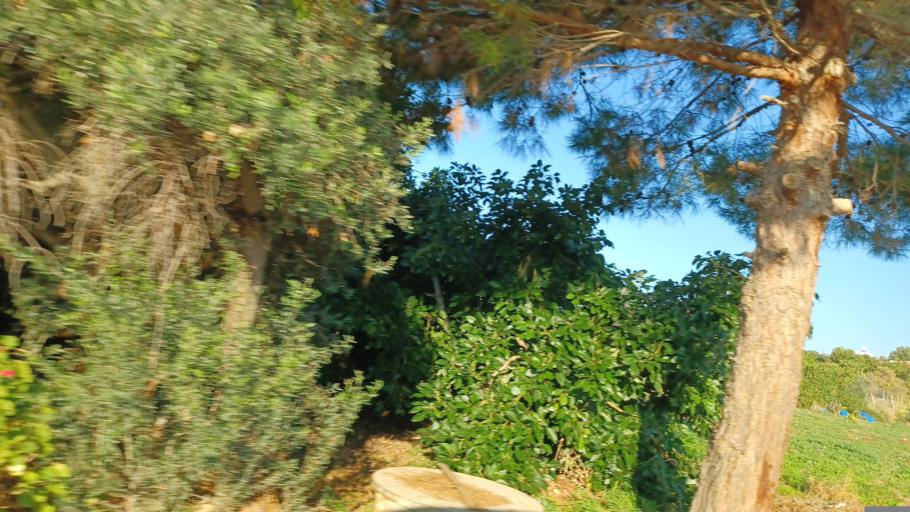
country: CY
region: Pafos
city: Pegeia
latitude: 34.8791
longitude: 32.3443
